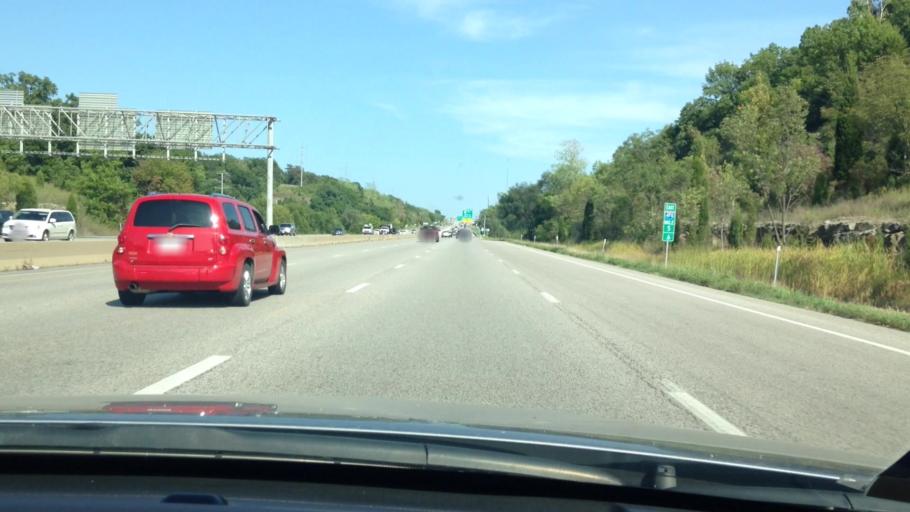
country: US
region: Missouri
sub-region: Jackson County
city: Lees Summit
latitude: 38.9358
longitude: -94.4431
